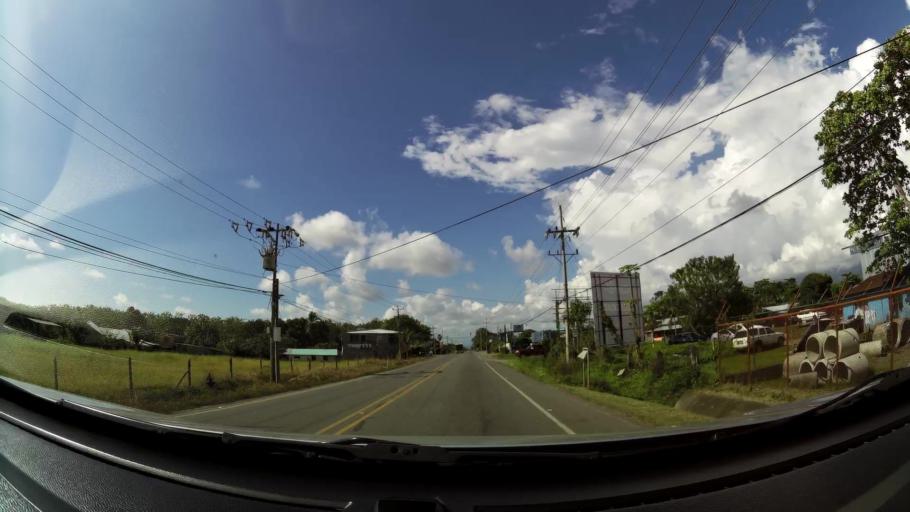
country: CR
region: Puntarenas
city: Quepos
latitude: 9.4595
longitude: -84.1803
